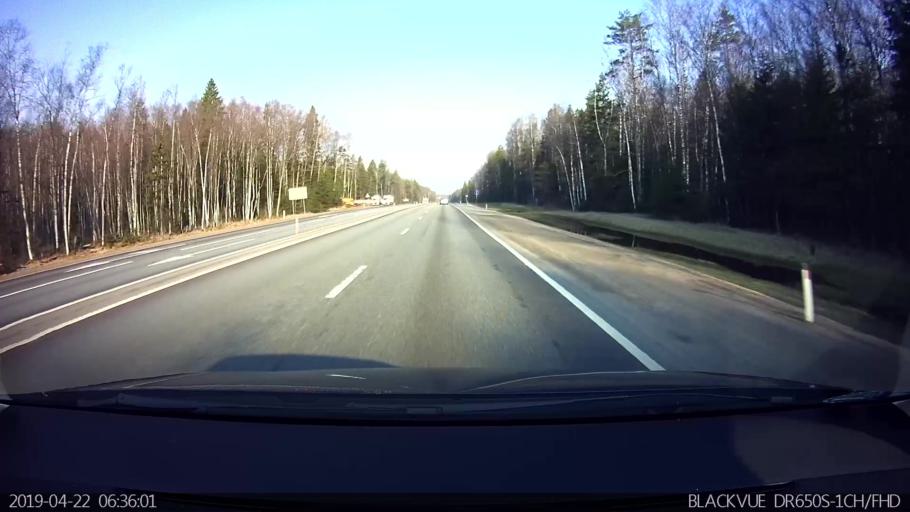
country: RU
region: Moskovskaya
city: Uvarovka
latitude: 55.4813
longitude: 35.4429
